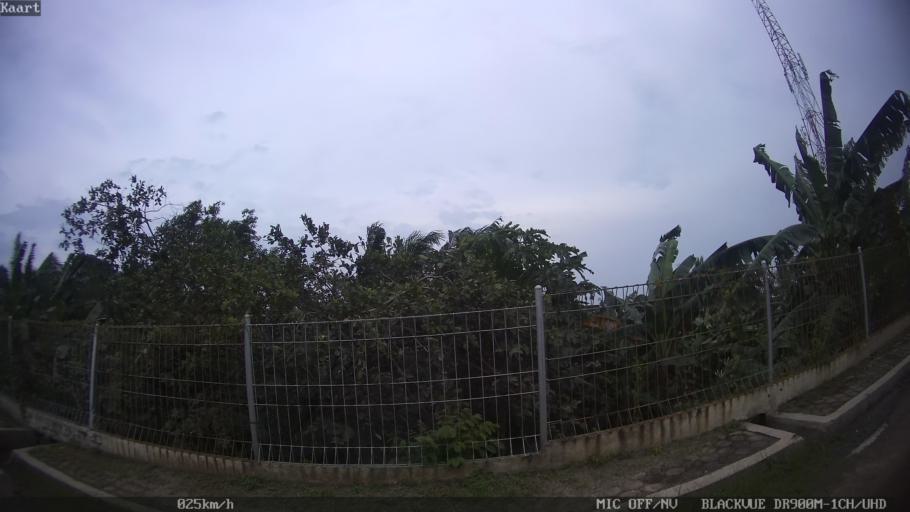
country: ID
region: Lampung
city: Kedaton
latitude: -5.3902
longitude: 105.2193
